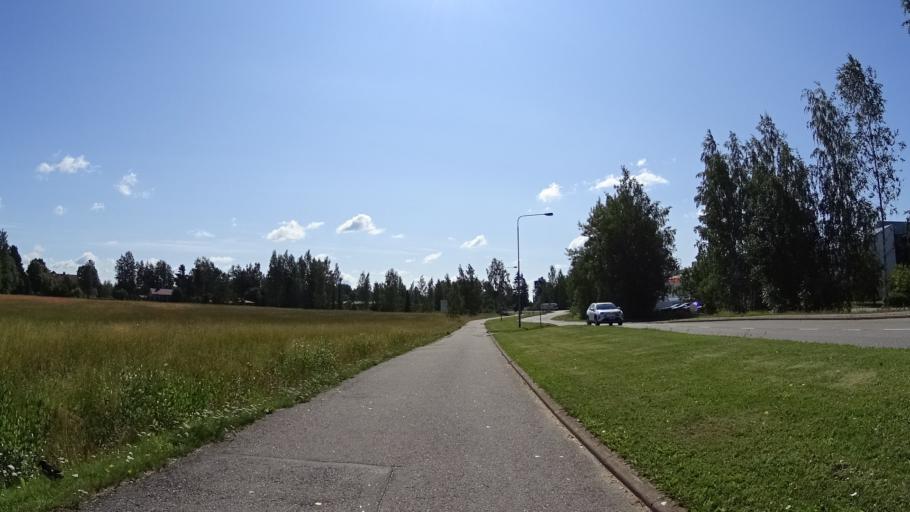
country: FI
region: Uusimaa
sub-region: Helsinki
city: Tuusula
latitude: 60.4119
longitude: 25.0394
